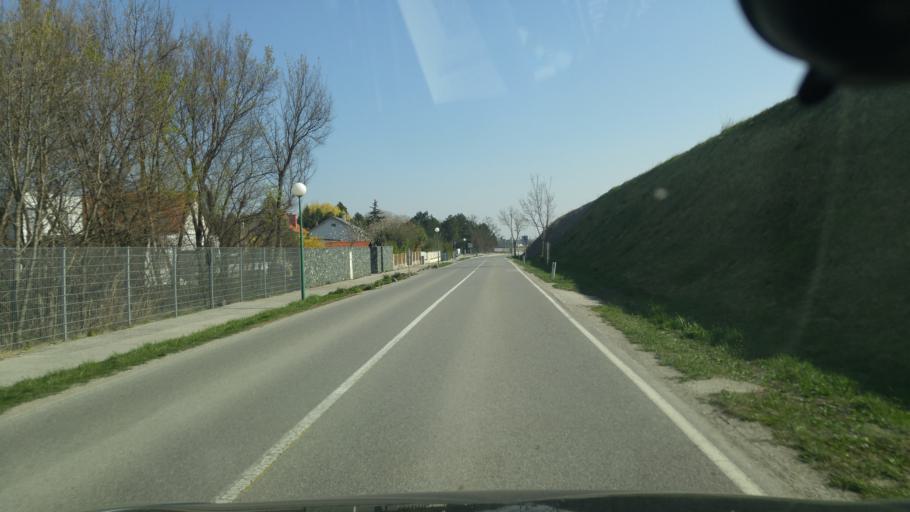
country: AT
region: Lower Austria
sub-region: Politischer Bezirk Baden
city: Trumau
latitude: 47.9839
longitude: 16.3339
